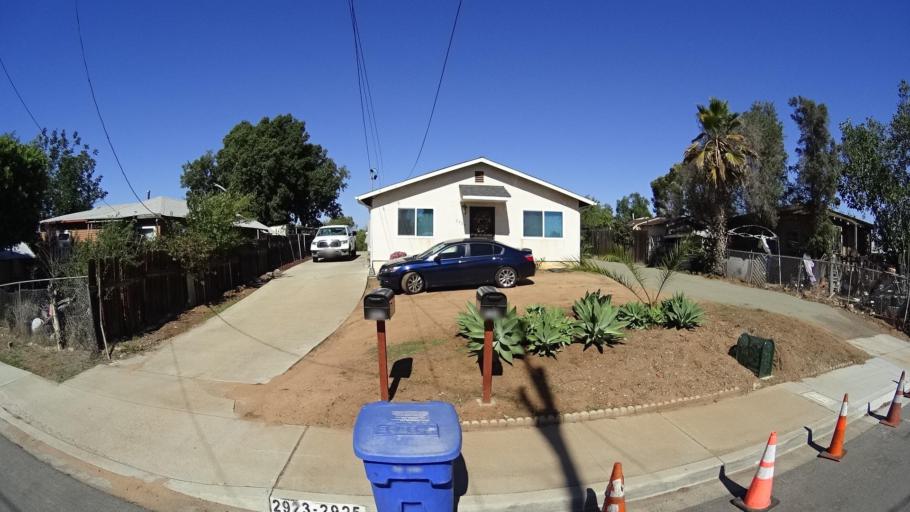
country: US
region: California
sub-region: San Diego County
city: Chula Vista
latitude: 32.6672
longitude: -117.0691
